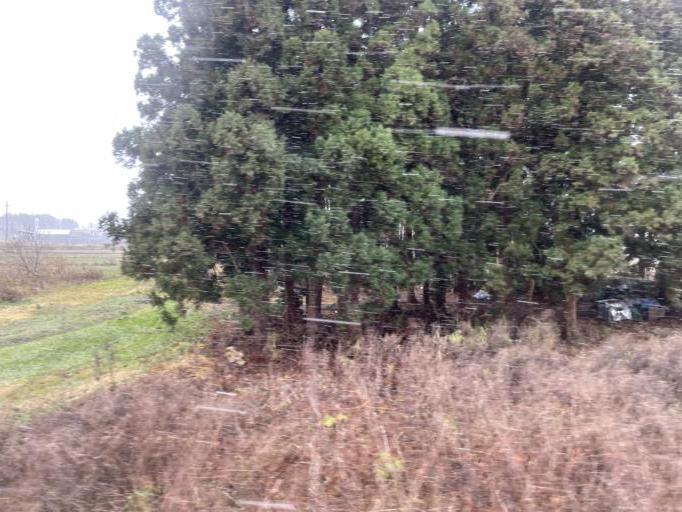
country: JP
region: Aomori
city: Aomori Shi
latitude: 40.9739
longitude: 140.6545
